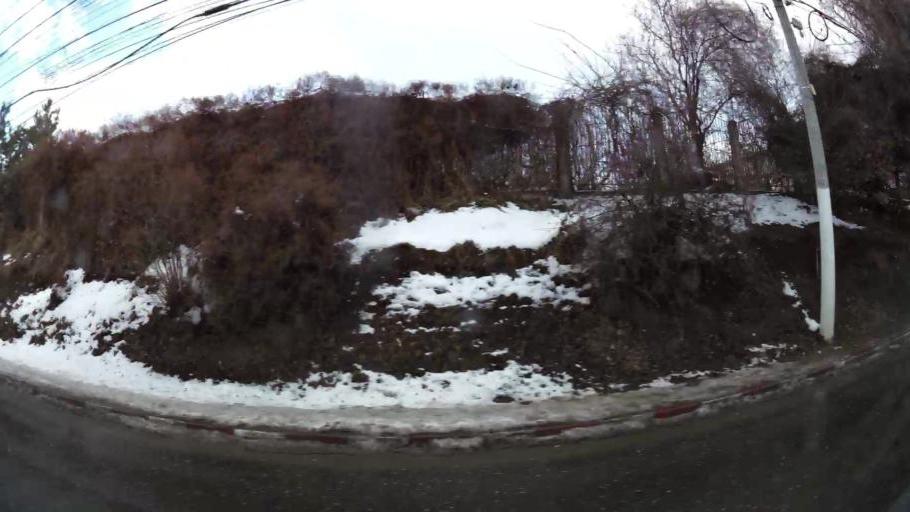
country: RO
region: Ilfov
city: Dobroesti
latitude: 44.4560
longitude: 26.1763
